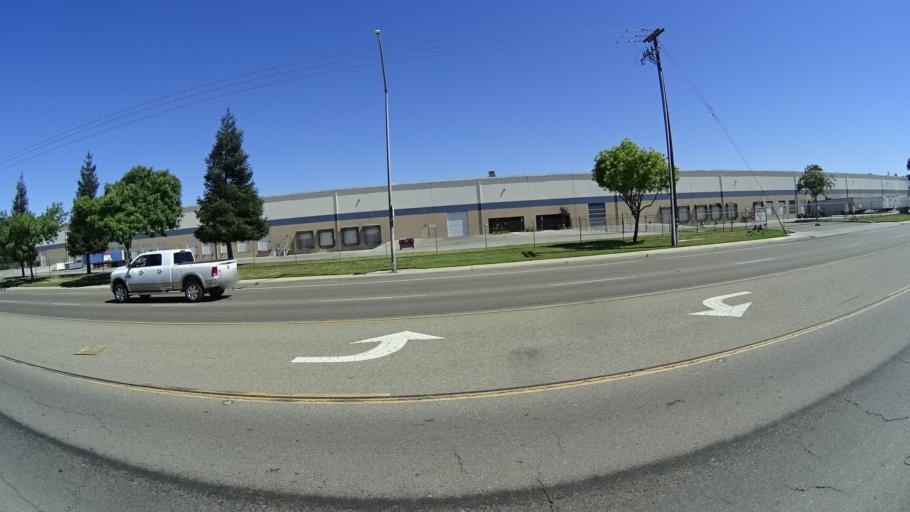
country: US
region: California
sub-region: Fresno County
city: Easton
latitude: 36.6920
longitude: -119.7803
